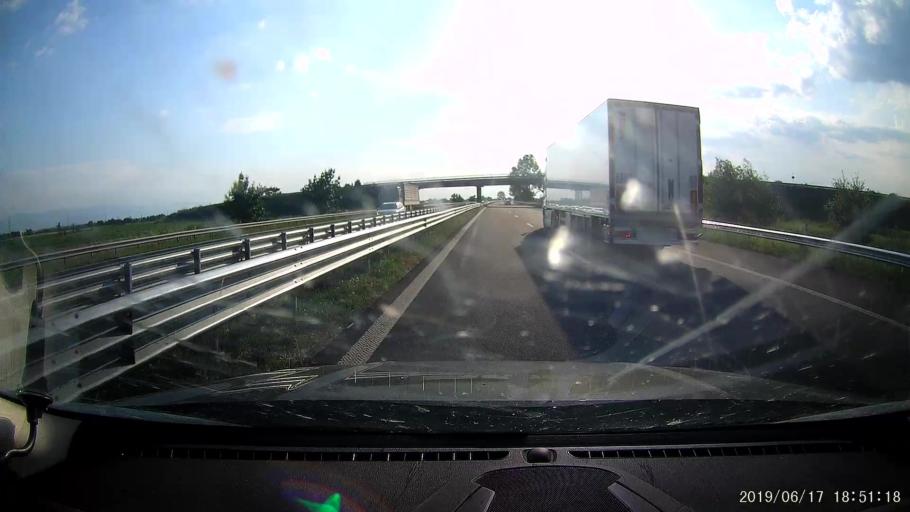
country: BG
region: Plovdiv
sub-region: Obshtina Rakovski
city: Rakovski
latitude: 42.2135
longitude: 24.9758
